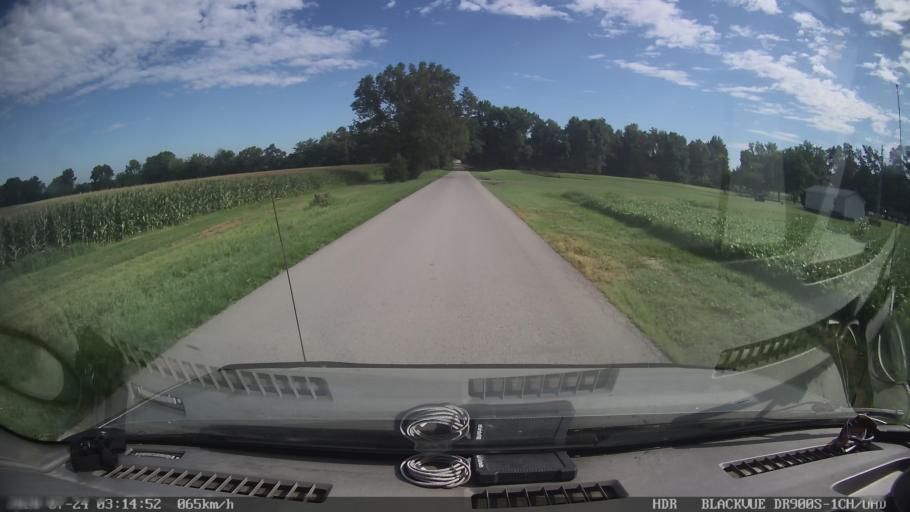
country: US
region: Kentucky
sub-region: Todd County
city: Guthrie
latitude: 36.6913
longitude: -87.1708
